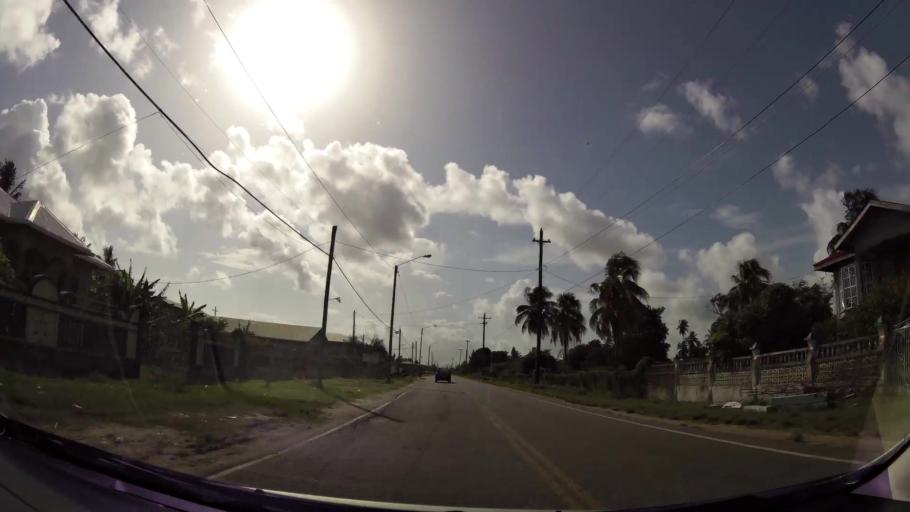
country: GY
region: Demerara-Mahaica
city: Mahaica Village
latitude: 6.7480
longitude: -57.9653
